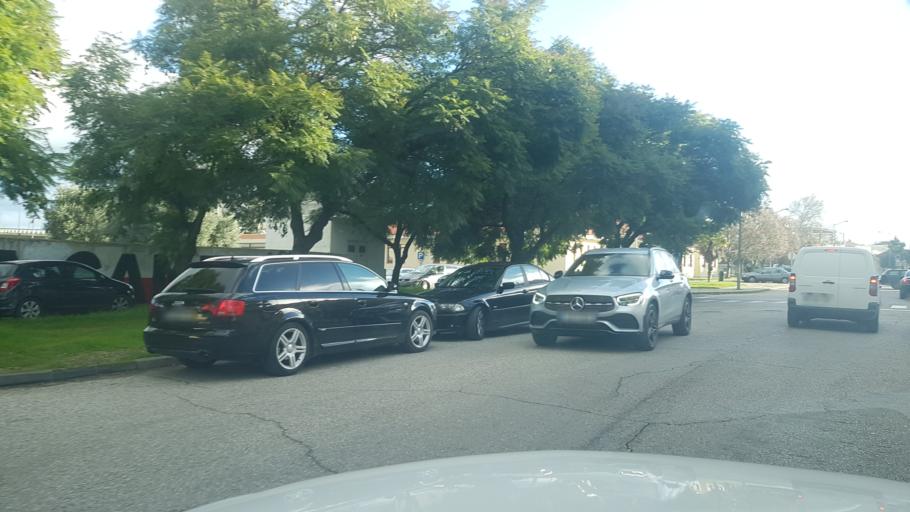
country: PT
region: Santarem
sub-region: Entroncamento
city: Entroncamento
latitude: 39.4668
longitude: -8.4720
